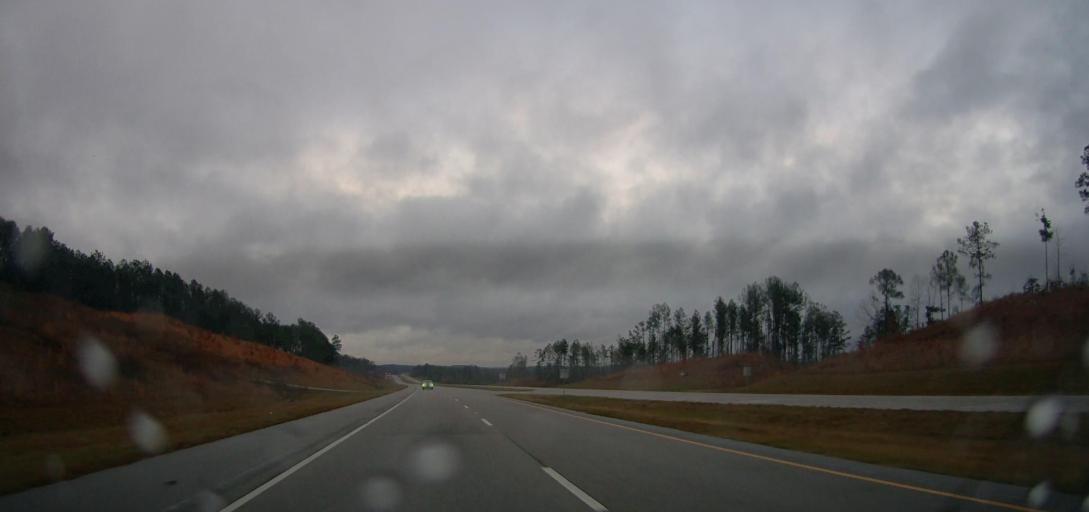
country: US
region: Alabama
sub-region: Bibb County
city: Centreville
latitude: 32.9477
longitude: -87.0980
